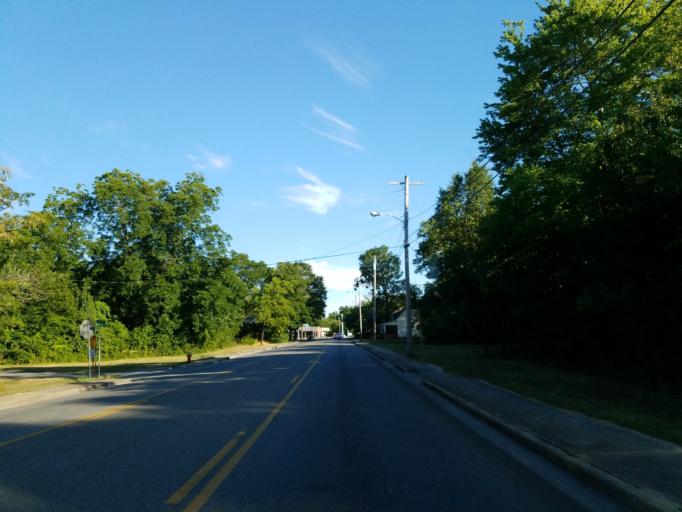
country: US
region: Georgia
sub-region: Gordon County
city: Calhoun
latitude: 34.5045
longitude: -84.9556
